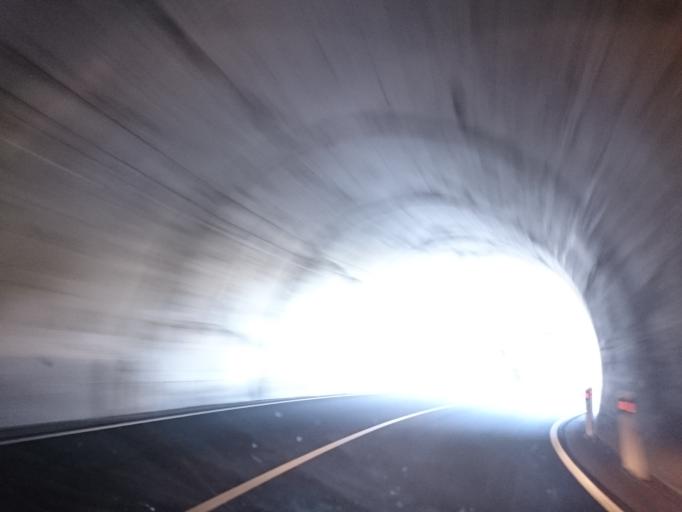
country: ES
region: Aragon
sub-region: Provincia de Huesca
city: Sopeira
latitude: 42.3260
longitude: 0.7421
